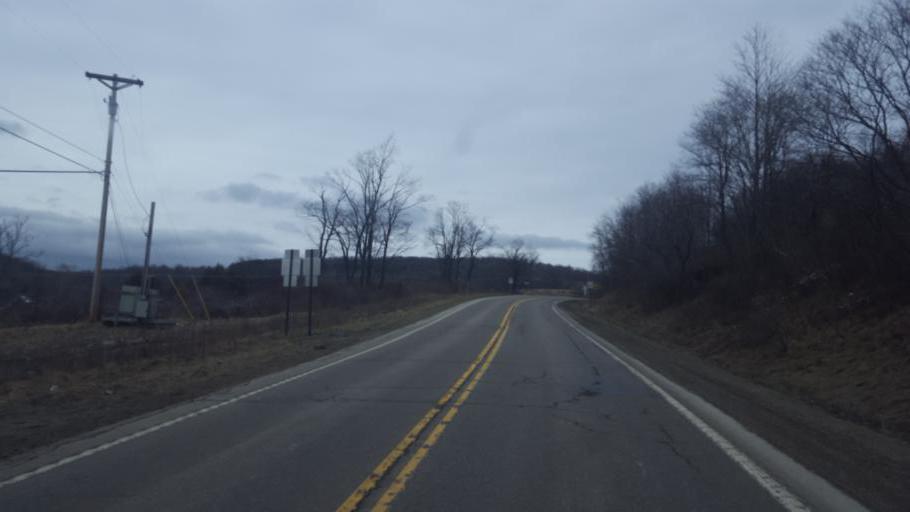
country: US
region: Pennsylvania
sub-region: Potter County
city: Coudersport
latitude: 41.8730
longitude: -77.8366
